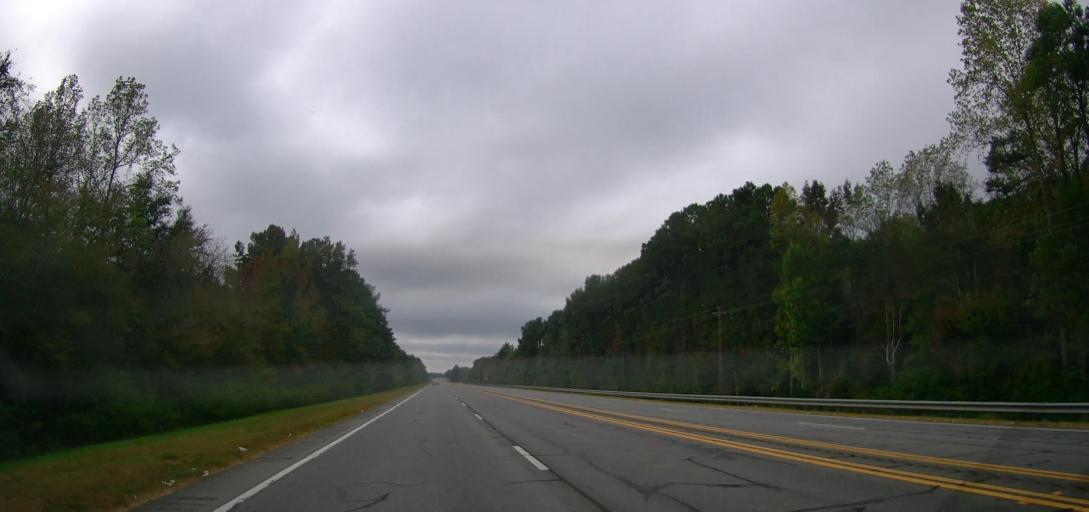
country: US
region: Georgia
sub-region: Tift County
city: Omega
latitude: 31.3251
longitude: -83.6201
